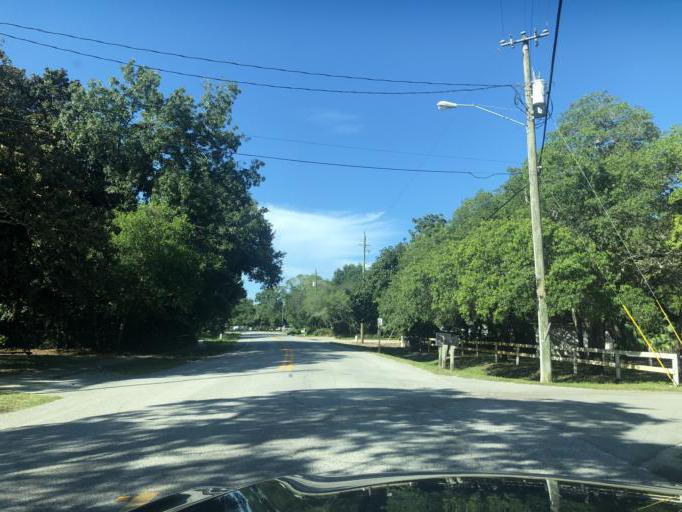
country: US
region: Florida
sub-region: Okaloosa County
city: Destin
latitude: 30.3997
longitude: -86.5112
